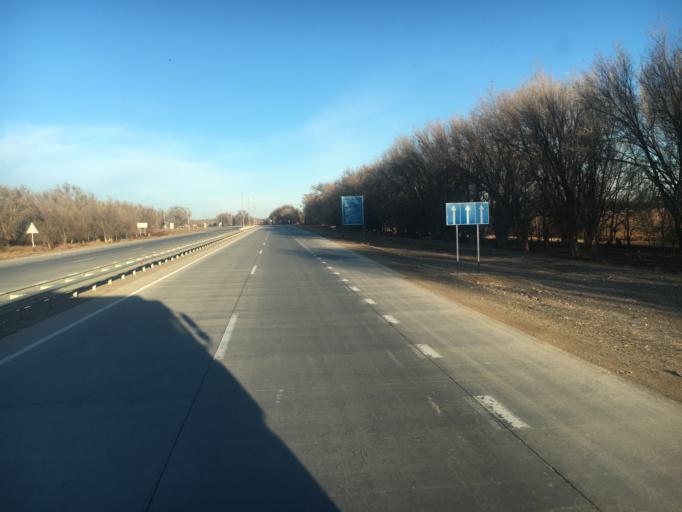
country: KZ
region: Ongtustik Qazaqstan
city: Turkestan
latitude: 43.1499
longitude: 68.5737
